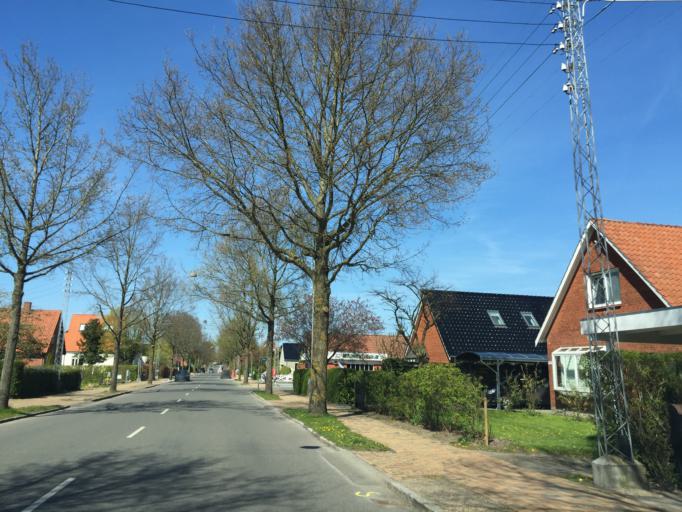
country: DK
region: South Denmark
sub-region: Odense Kommune
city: Odense
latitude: 55.3746
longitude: 10.3880
